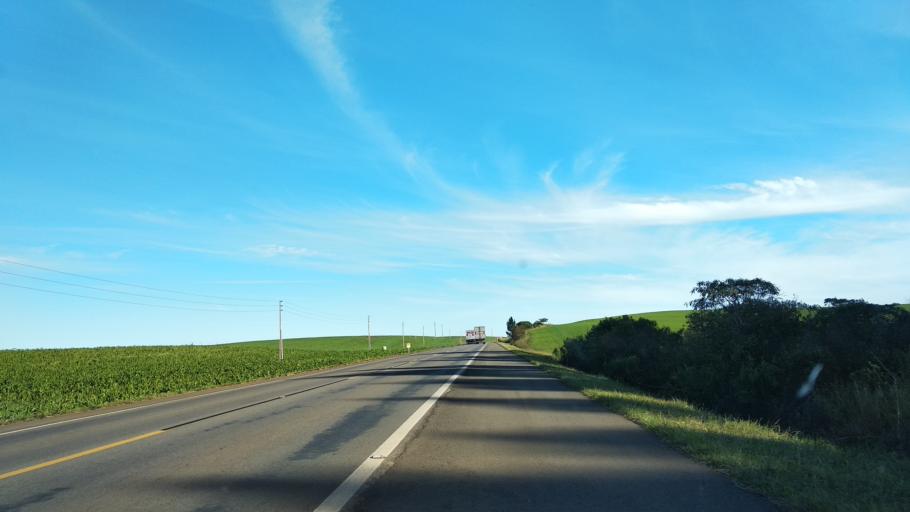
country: BR
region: Santa Catarina
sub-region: Celso Ramos
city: Celso Ramos
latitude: -27.5164
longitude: -51.3499
